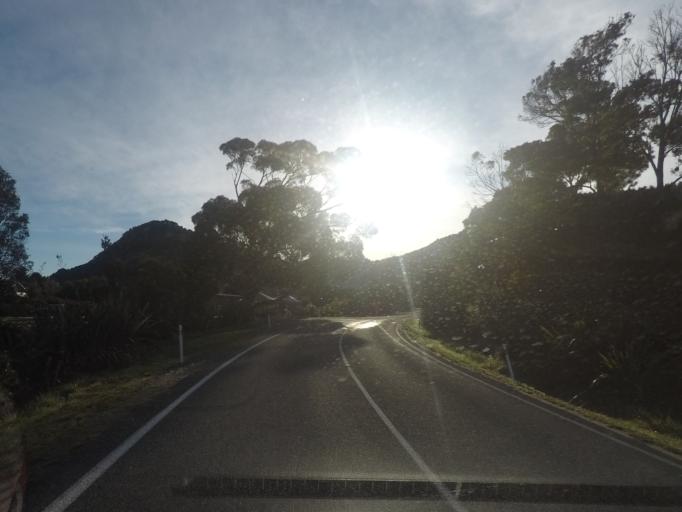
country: NZ
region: Tasman
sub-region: Tasman District
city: Takaka
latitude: -40.8125
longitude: 172.9161
